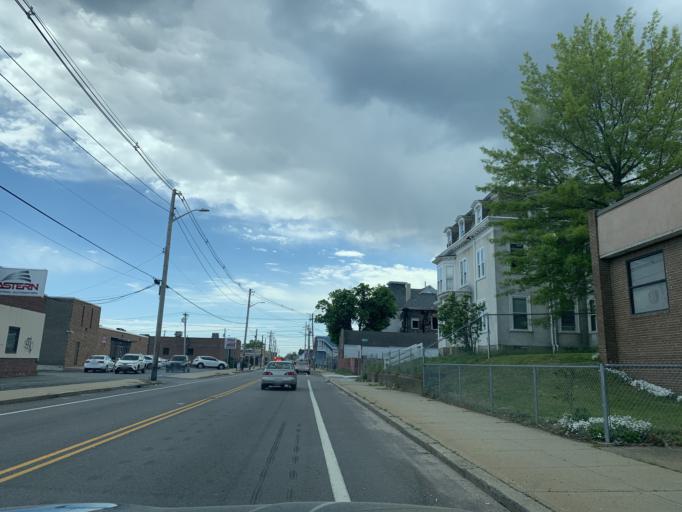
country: US
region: Rhode Island
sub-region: Providence County
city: Providence
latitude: 41.8046
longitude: -71.4071
